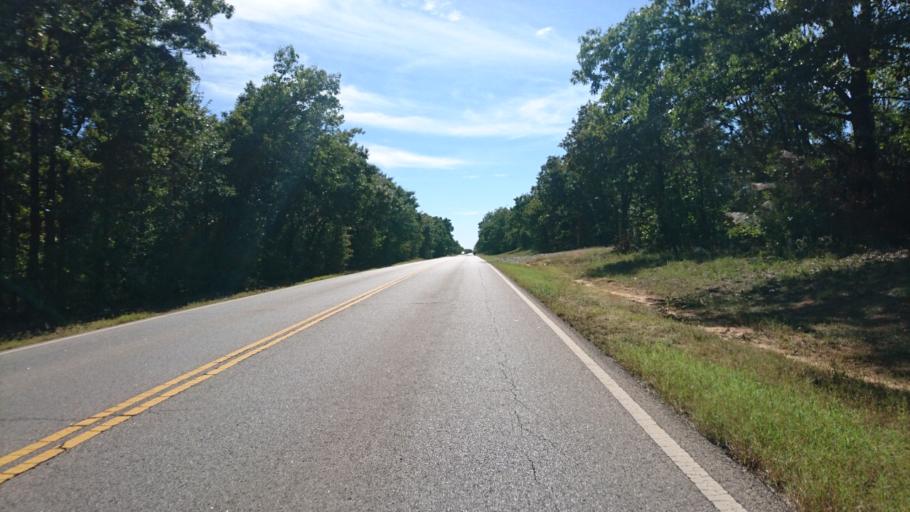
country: US
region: Oklahoma
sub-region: Lincoln County
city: Stroud
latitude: 35.7323
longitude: -96.7239
